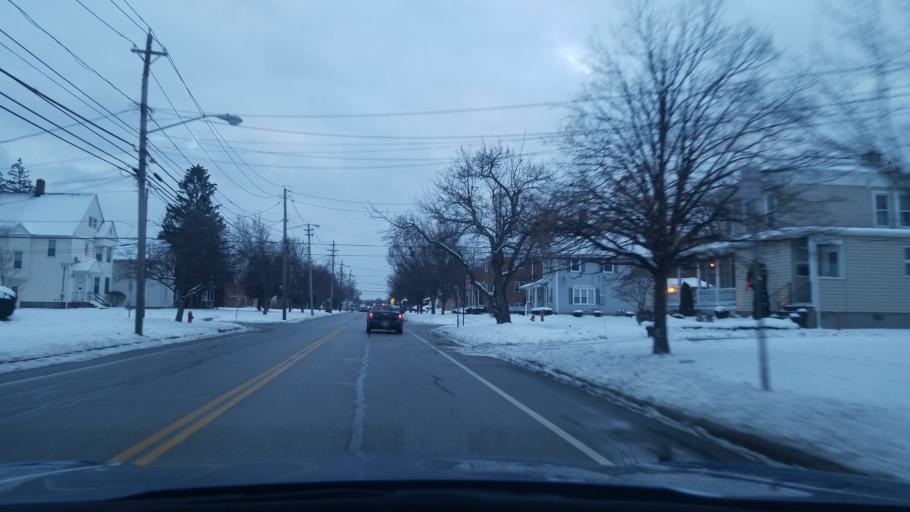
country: US
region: Ohio
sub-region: Cuyahoga County
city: Berea
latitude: 41.3766
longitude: -81.8531
